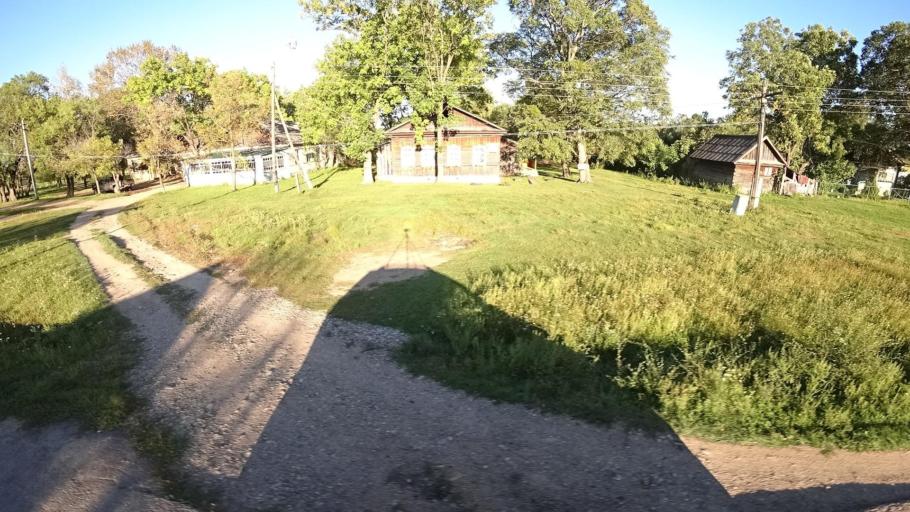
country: RU
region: Primorskiy
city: Kirovskiy
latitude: 44.8305
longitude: 133.5753
